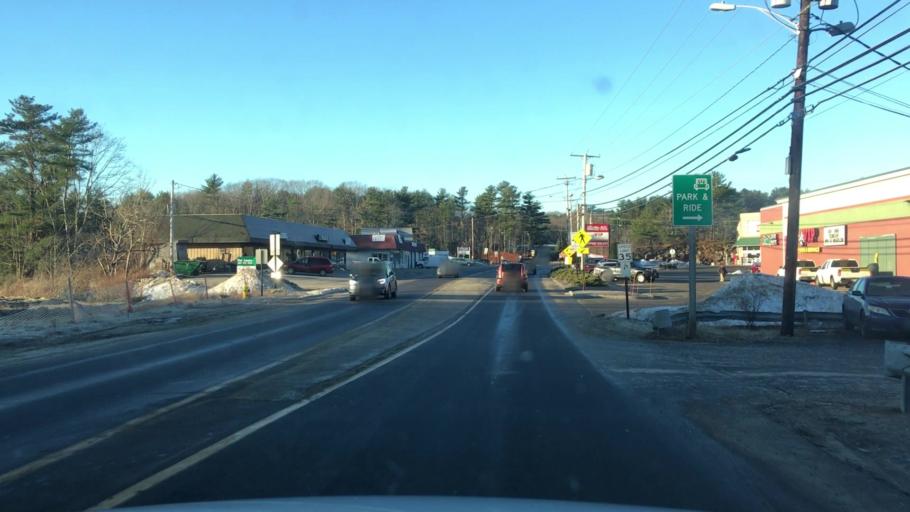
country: US
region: Maine
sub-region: Sagadahoc County
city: Bath
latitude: 43.9067
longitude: -69.8300
